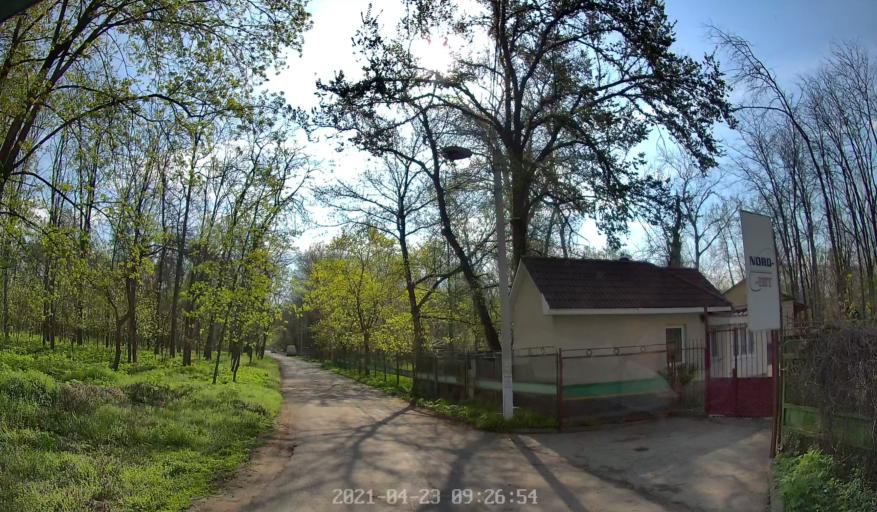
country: MD
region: Chisinau
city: Vadul lui Voda
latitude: 47.0864
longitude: 29.0967
